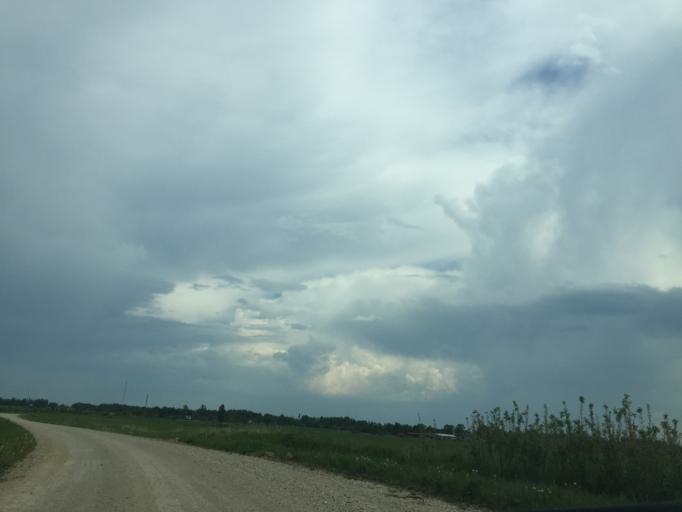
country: LV
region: Livani
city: Livani
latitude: 56.5494
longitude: 26.2305
